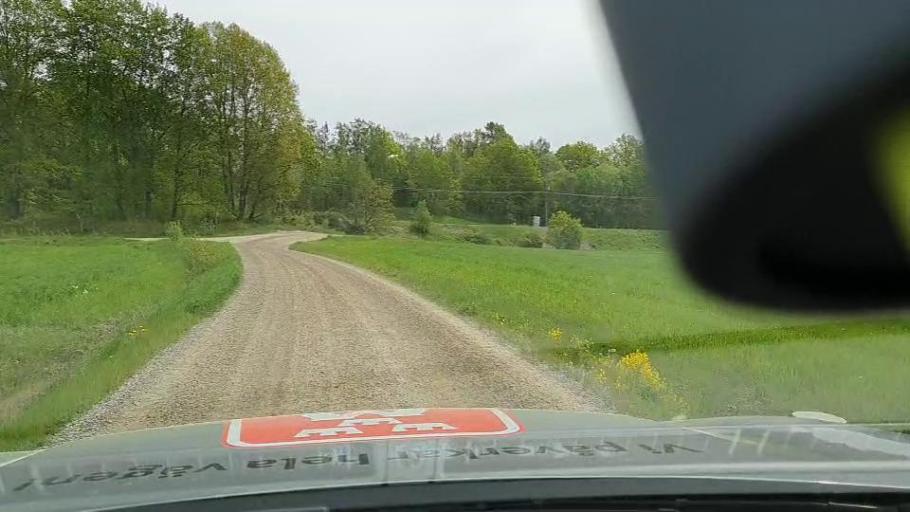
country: SE
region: Soedermanland
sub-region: Flens Kommun
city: Flen
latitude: 59.0408
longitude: 16.5791
